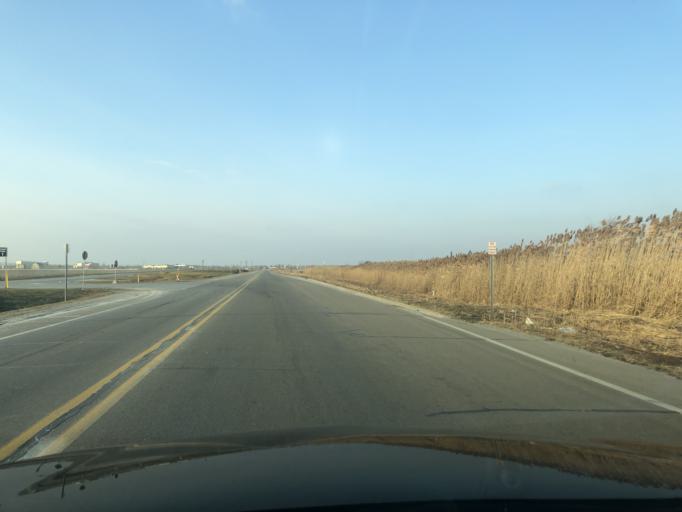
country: US
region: Michigan
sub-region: Wayne County
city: Romulus
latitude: 42.2359
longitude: -83.3439
